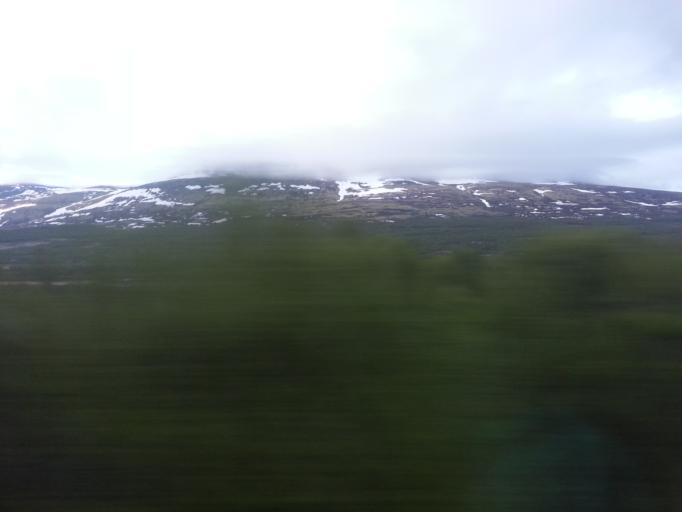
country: NO
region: Oppland
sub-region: Dovre
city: Dovre
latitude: 62.1496
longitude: 9.3196
